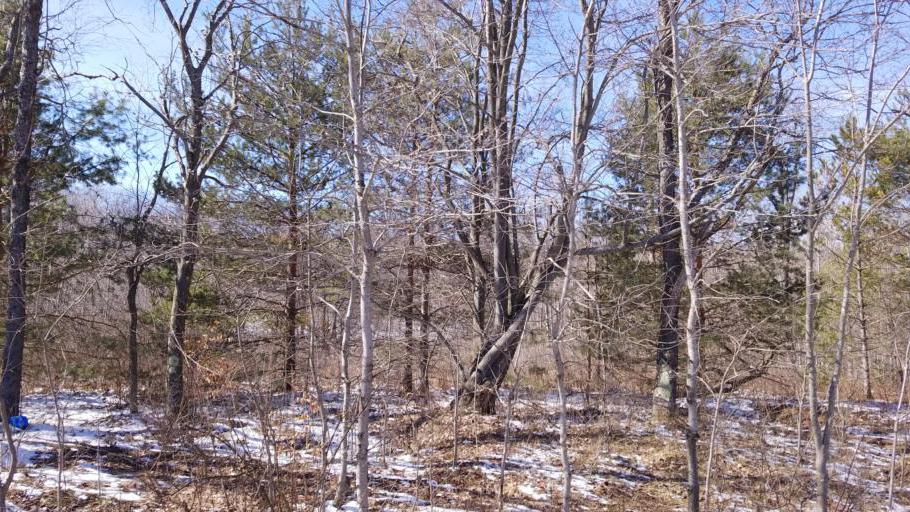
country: US
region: Pennsylvania
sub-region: Potter County
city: Galeton
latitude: 41.9098
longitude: -77.7473
